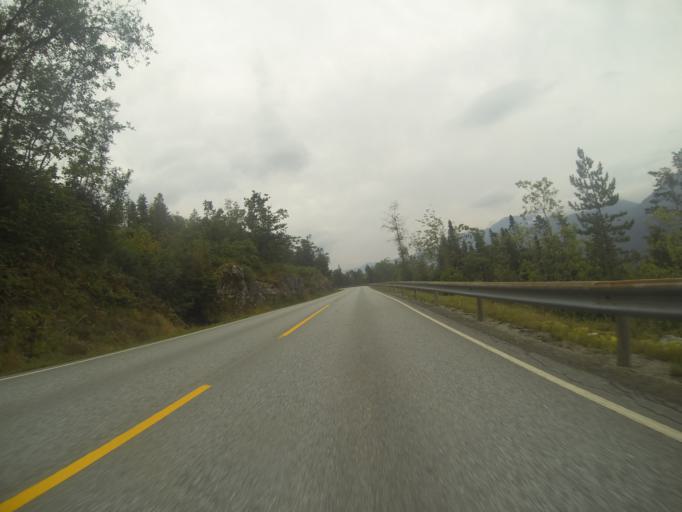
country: NO
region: Rogaland
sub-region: Suldal
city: Sand
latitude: 59.5540
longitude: 6.2616
